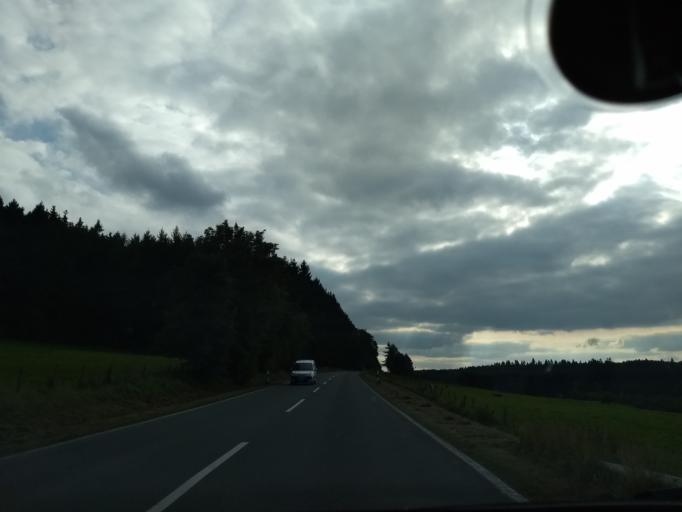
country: DE
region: North Rhine-Westphalia
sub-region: Regierungsbezirk Arnsberg
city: Olsberg
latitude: 51.4049
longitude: 8.5063
